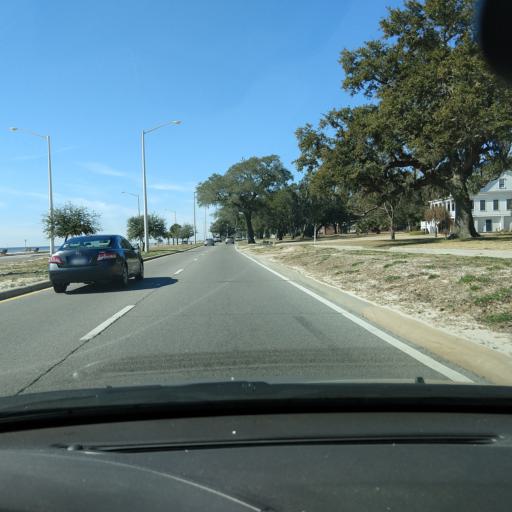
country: US
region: Mississippi
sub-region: Harrison County
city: Biloxi
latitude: 30.3947
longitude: -88.9178
